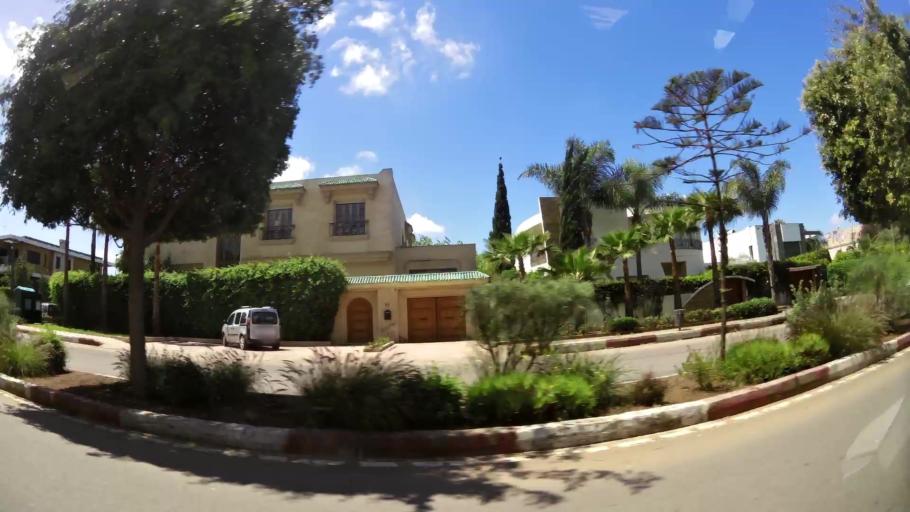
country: MA
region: Grand Casablanca
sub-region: Casablanca
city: Casablanca
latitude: 33.5287
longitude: -7.6306
